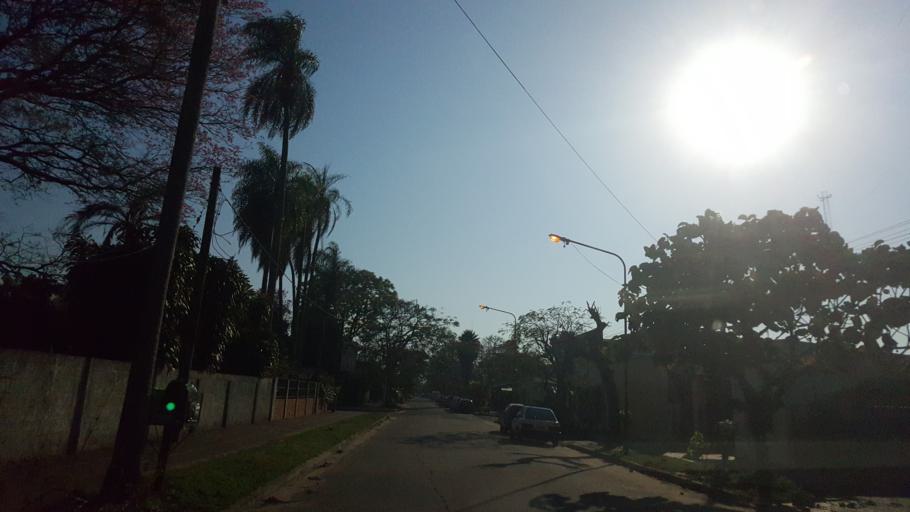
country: AR
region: Corrientes
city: Ituzaingo
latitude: -27.5842
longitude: -56.6854
